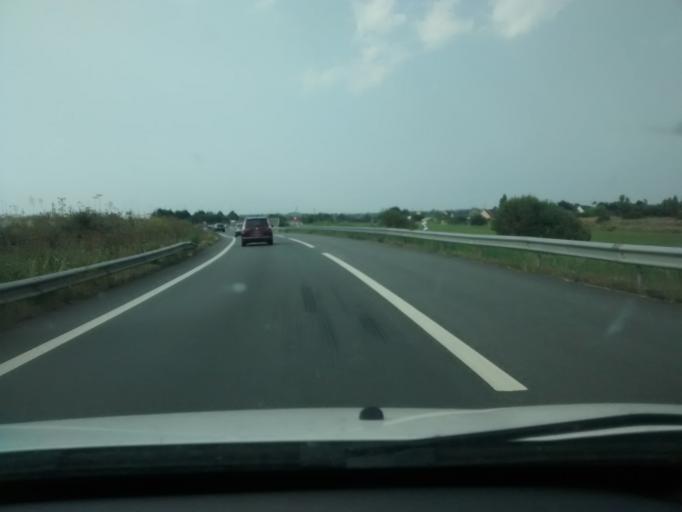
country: FR
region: Pays de la Loire
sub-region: Departement de la Loire-Atlantique
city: Trignac
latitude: 47.3066
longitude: -2.2087
